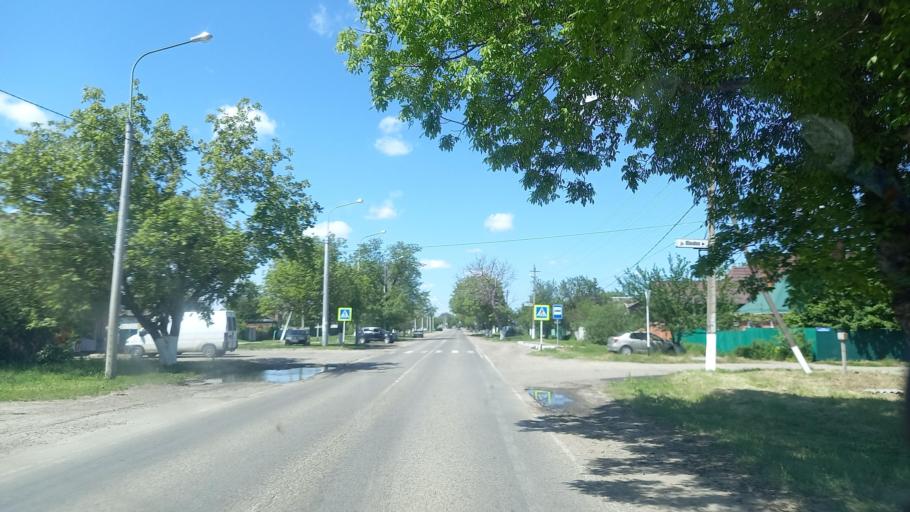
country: RU
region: Krasnodarskiy
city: Novoukrainskoye
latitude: 45.3804
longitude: 40.5157
